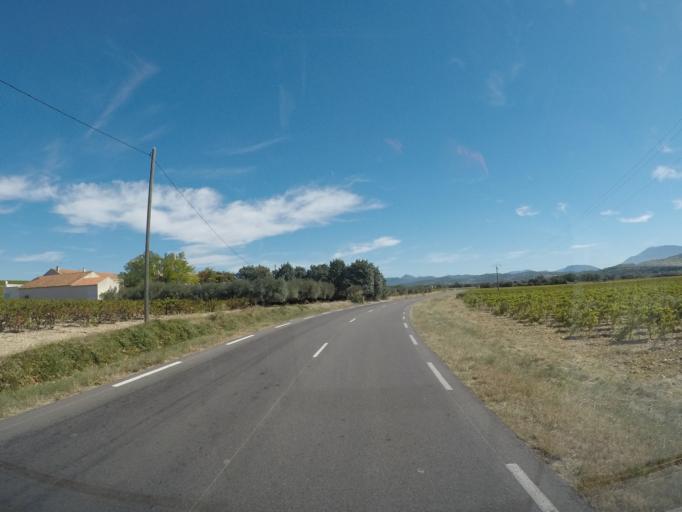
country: FR
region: Provence-Alpes-Cote d'Azur
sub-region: Departement du Vaucluse
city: Visan
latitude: 44.2908
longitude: 4.9651
